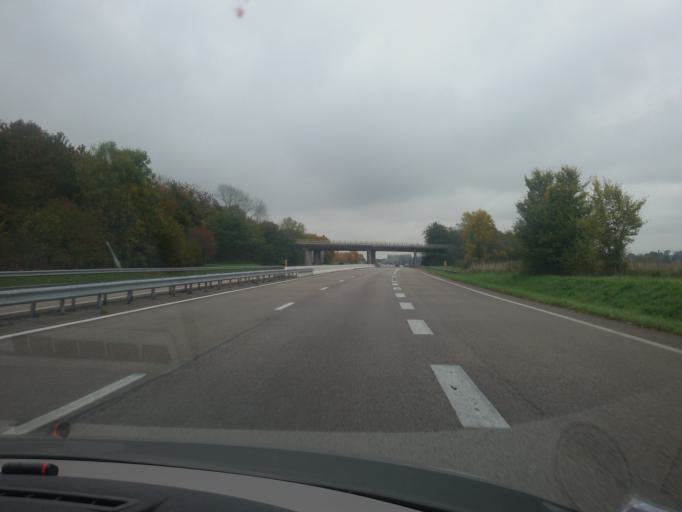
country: FR
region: Haute-Normandie
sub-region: Departement de l'Eure
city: Corneville-sur-Risle
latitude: 49.3827
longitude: 0.6039
